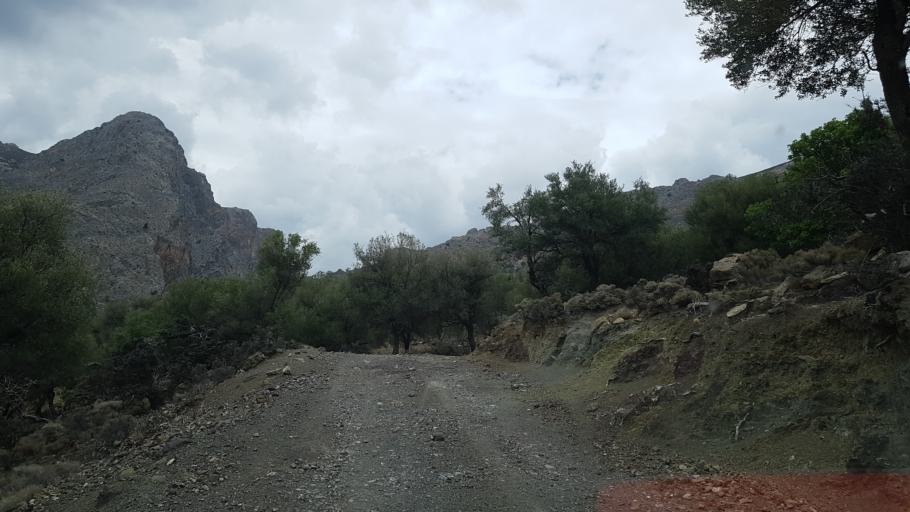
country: GR
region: Crete
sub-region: Nomos Irakleiou
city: Agioi Deka
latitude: 34.9448
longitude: 24.9927
